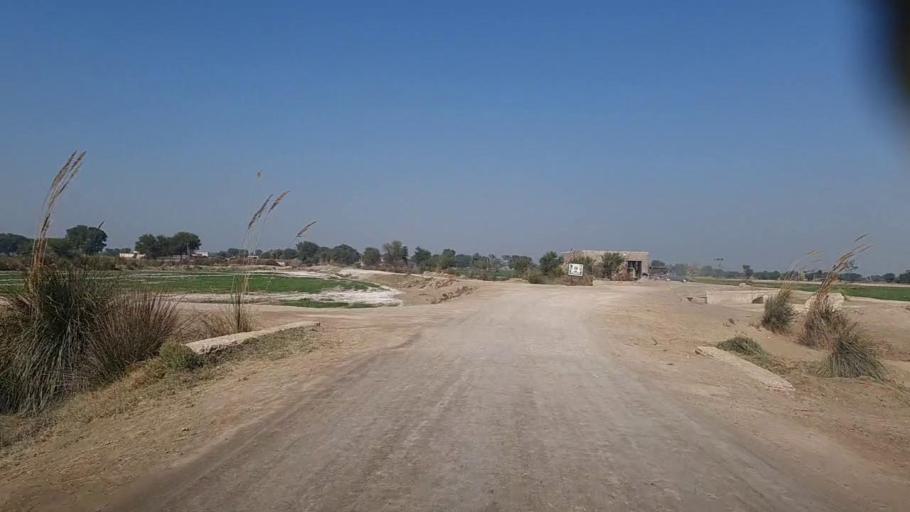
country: PK
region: Sindh
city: Khairpur
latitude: 27.9923
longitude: 69.8474
